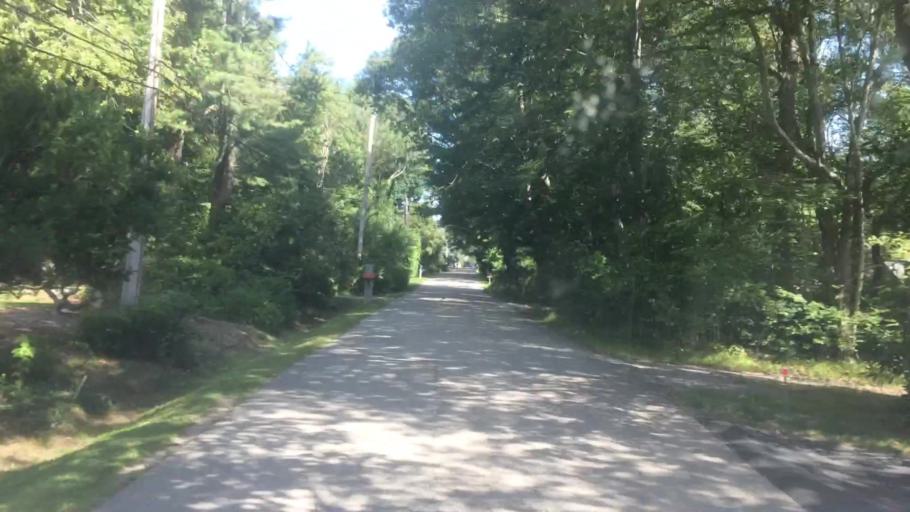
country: US
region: Rhode Island
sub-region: Newport County
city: Jamestown
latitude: 41.5028
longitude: -71.4216
